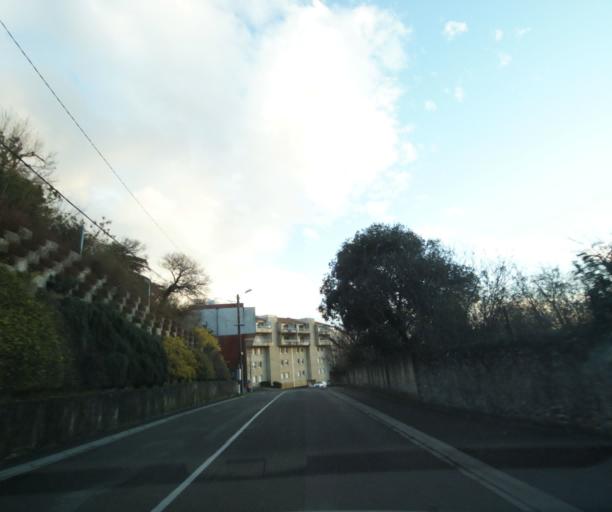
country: FR
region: Rhone-Alpes
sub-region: Departement de la Drome
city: Valence
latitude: 44.9441
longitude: 4.9025
